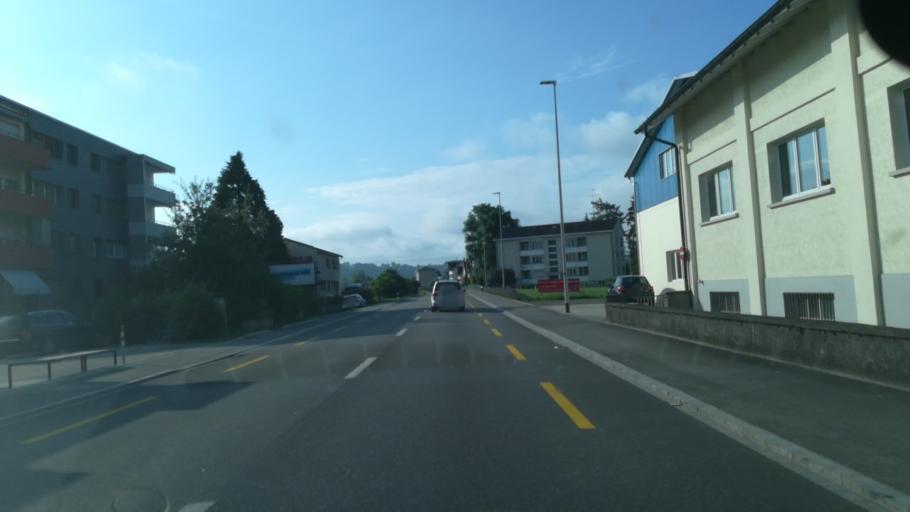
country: CH
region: Thurgau
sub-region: Weinfelden District
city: Sulgen
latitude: 47.5327
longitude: 9.1886
